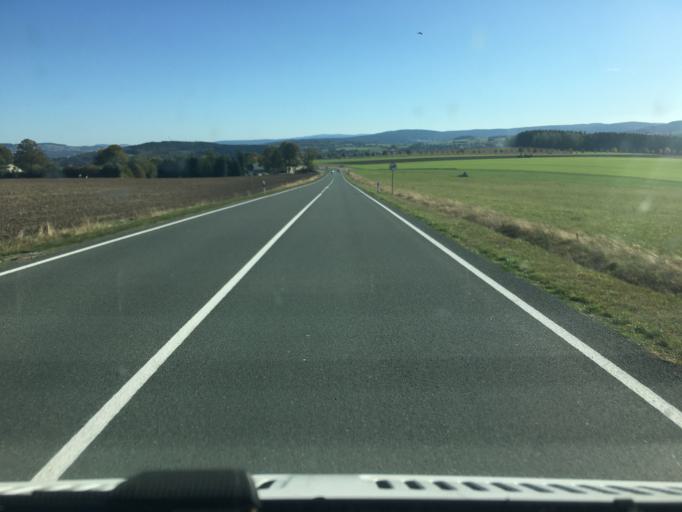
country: DE
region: Saxony
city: Schneeberg
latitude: 50.6052
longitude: 12.6053
